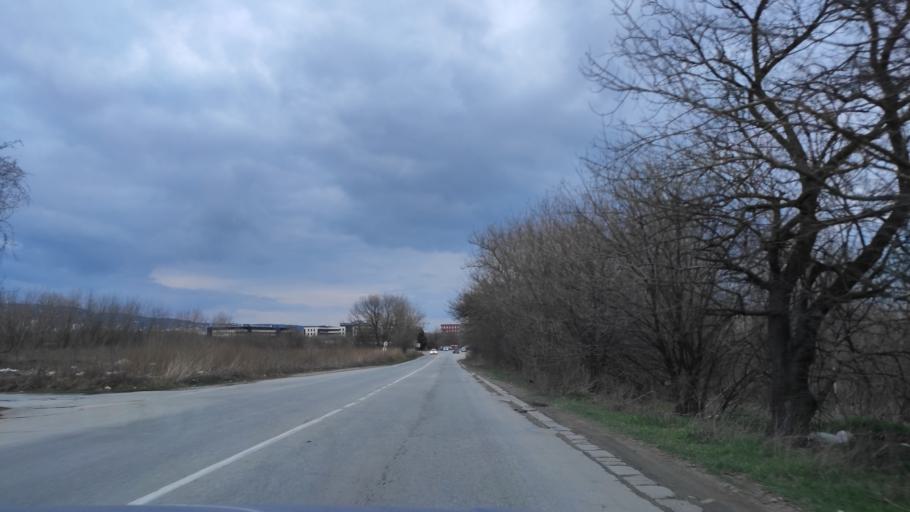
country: BG
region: Varna
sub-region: Obshtina Aksakovo
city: Aksakovo
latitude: 43.2277
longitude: 27.8495
